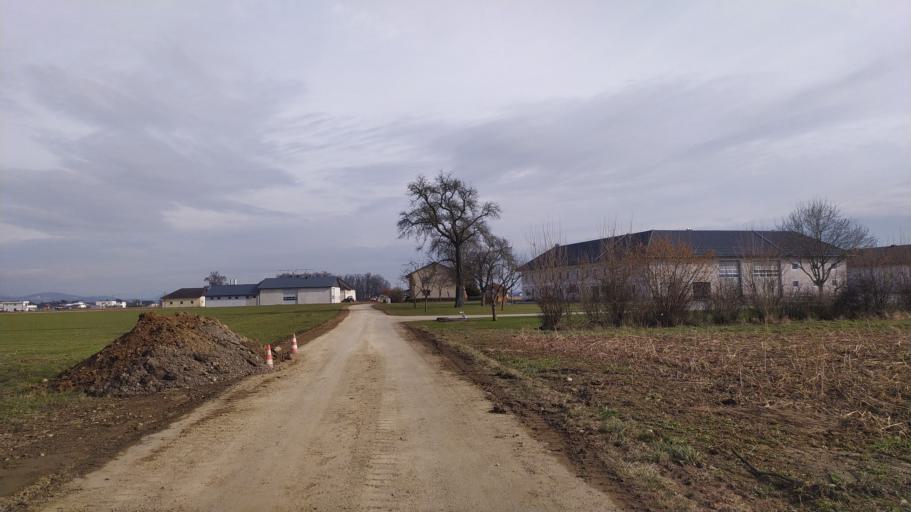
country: AT
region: Upper Austria
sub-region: Politischer Bezirk Perg
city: Perg
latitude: 48.1922
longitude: 14.6734
